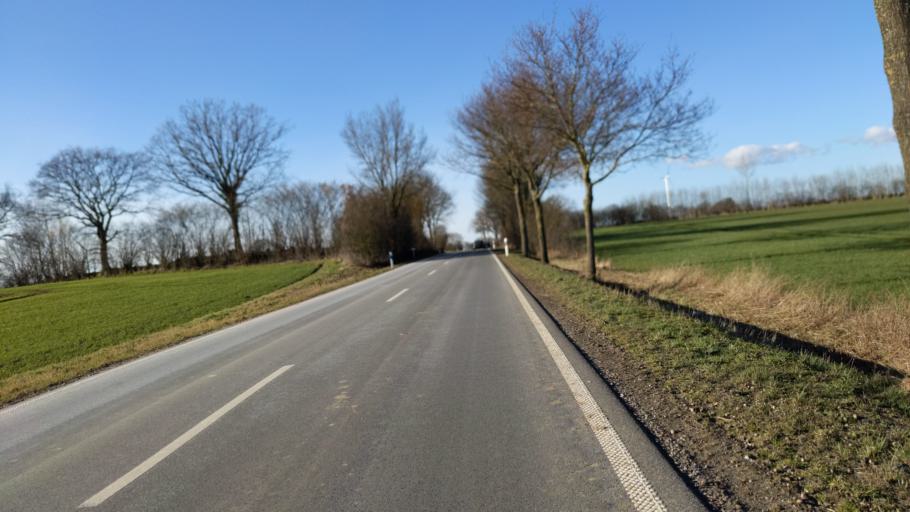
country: DE
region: Schleswig-Holstein
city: Susel
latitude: 54.0493
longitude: 10.6564
